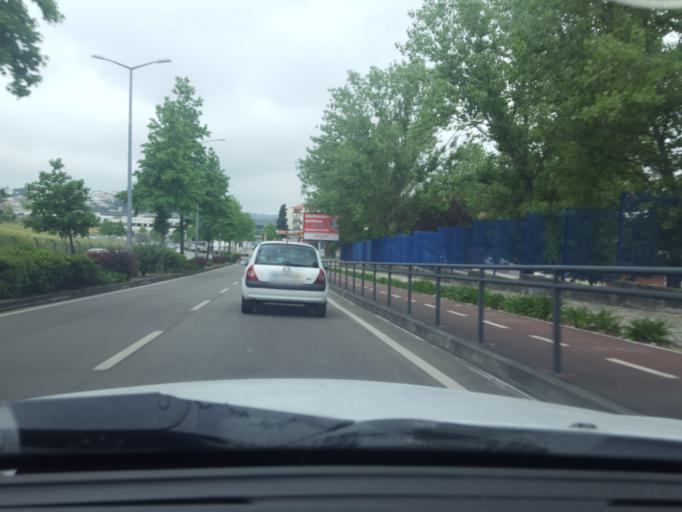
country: PT
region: Leiria
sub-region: Leiria
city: Leiria
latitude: 39.7379
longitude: -8.8138
